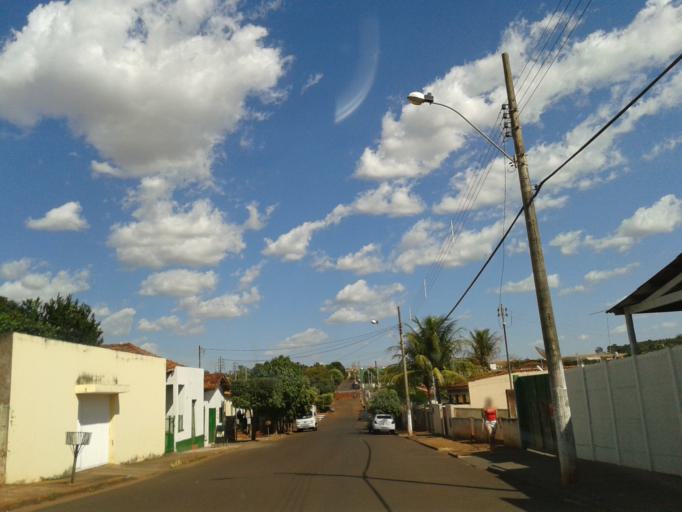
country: BR
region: Minas Gerais
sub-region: Capinopolis
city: Capinopolis
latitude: -18.6844
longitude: -49.5726
